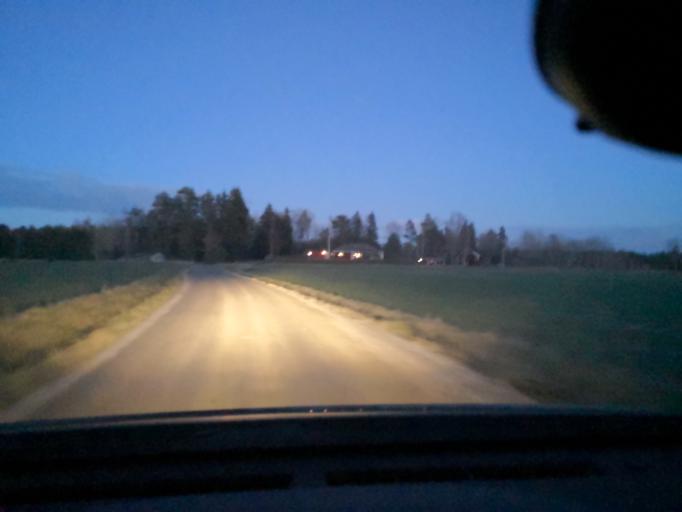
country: SE
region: Vaestmanland
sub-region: Sala Kommun
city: Sala
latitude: 59.8755
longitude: 16.7267
